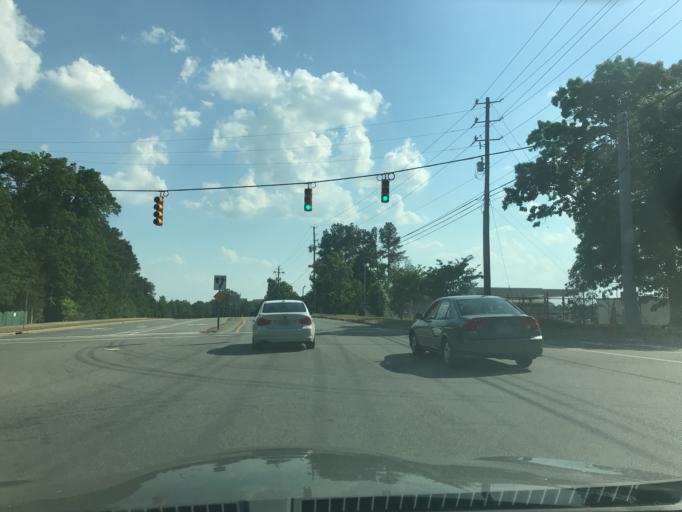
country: US
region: North Carolina
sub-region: Wake County
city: Wake Forest
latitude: 35.9168
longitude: -78.5943
